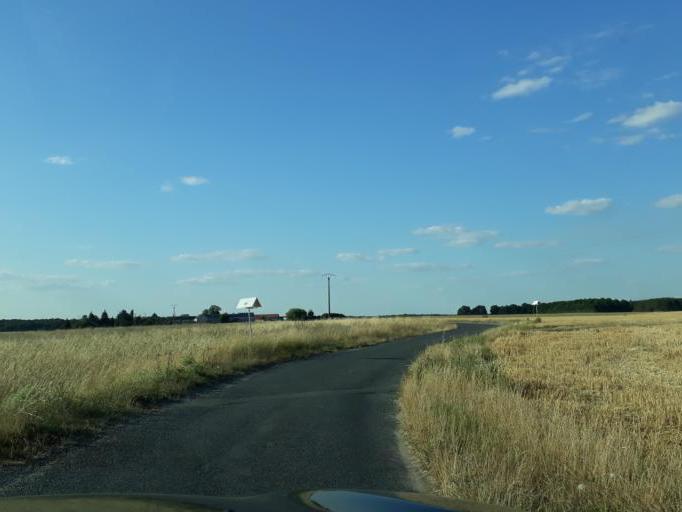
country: FR
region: Centre
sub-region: Departement du Loiret
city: Chaingy
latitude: 47.8967
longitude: 1.7611
